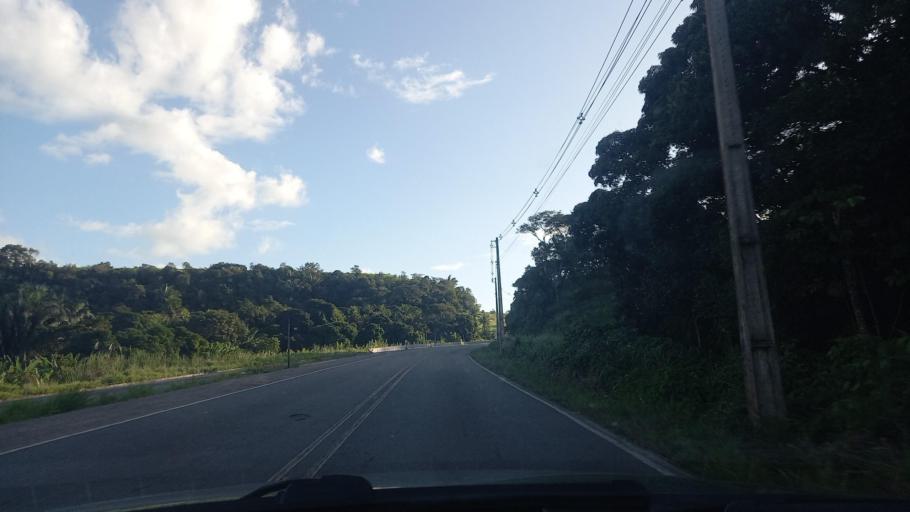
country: BR
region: Alagoas
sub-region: Sao Miguel Dos Campos
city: Sao Miguel dos Campos
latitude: -9.8206
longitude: -36.2205
